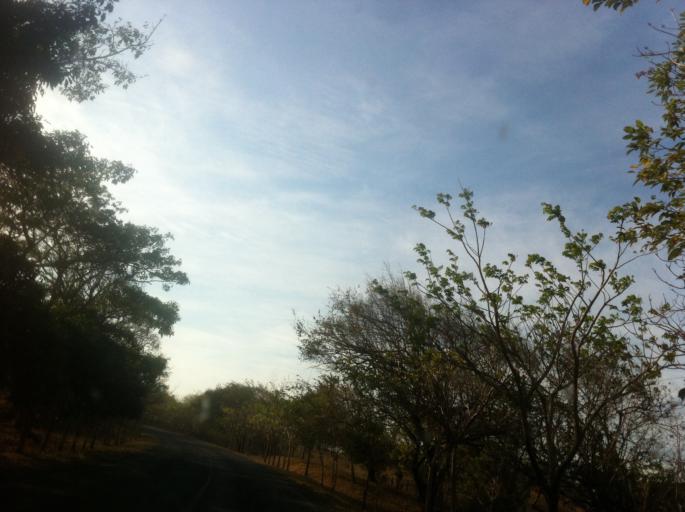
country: NI
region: Rivas
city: San Juan del Sur
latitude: 11.2980
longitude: -85.6880
